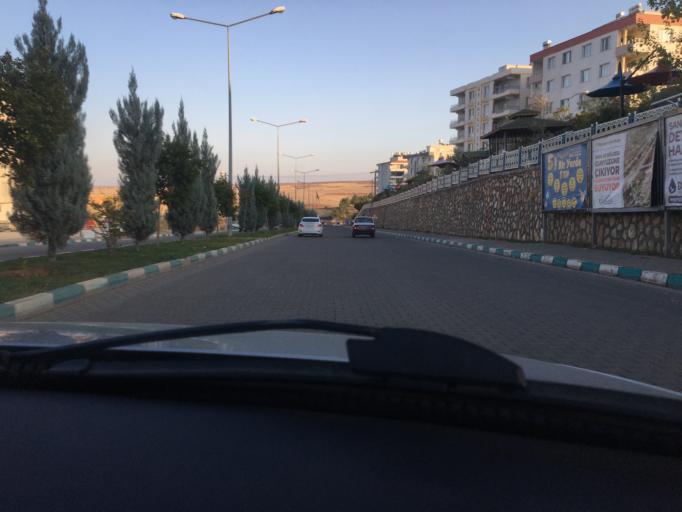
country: TR
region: Sanliurfa
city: Halfeti
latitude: 37.2303
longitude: 37.9479
